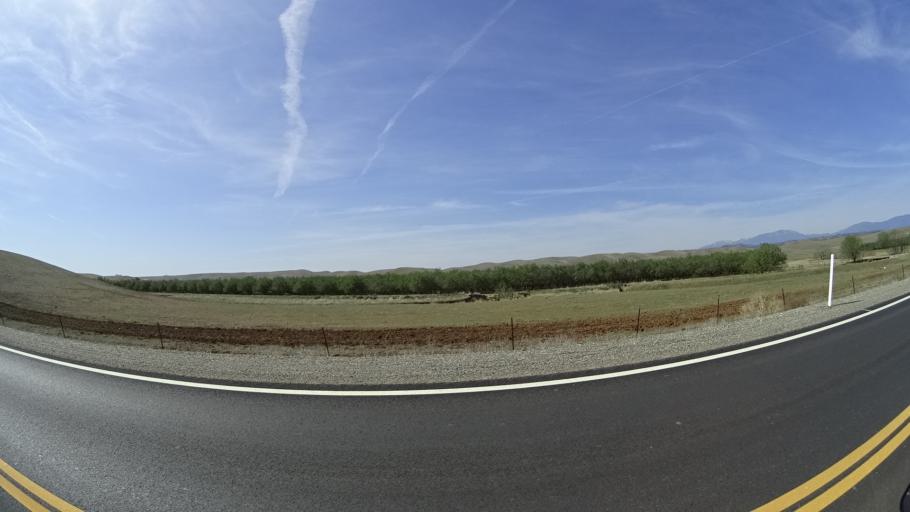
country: US
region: California
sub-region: Glenn County
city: Willows
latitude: 39.5319
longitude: -122.3398
